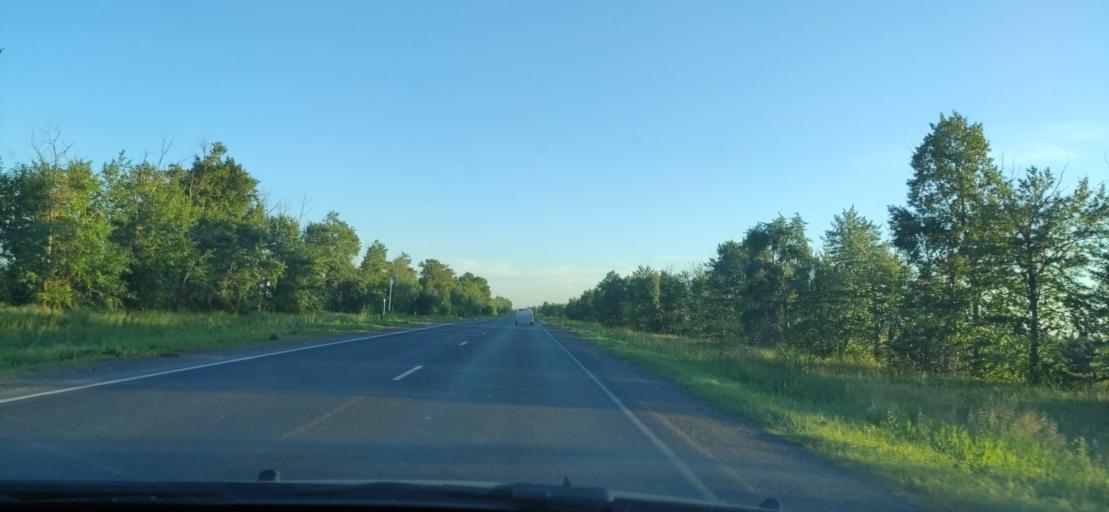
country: RU
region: Ulyanovsk
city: Cherdakly
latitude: 54.4054
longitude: 48.8693
